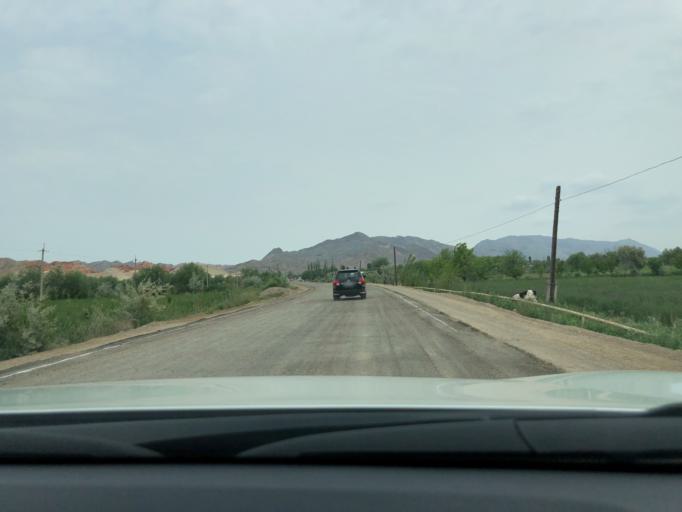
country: TJ
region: Viloyati Sughd
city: Isfara
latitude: 40.1535
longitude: 70.6261
